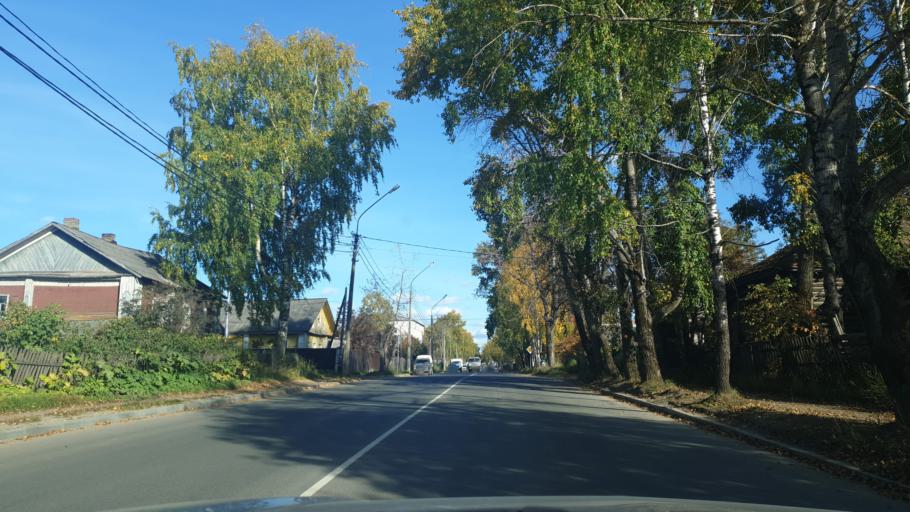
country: RU
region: Komi Republic
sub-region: Syktyvdinskiy Rayon
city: Syktyvkar
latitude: 61.6849
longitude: 50.8013
